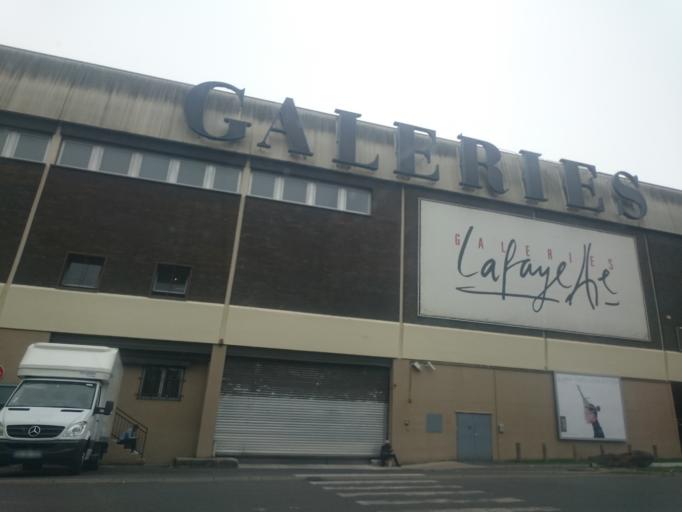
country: FR
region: Ile-de-France
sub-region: Departement de l'Essonne
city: Evry
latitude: 48.6303
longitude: 2.4284
